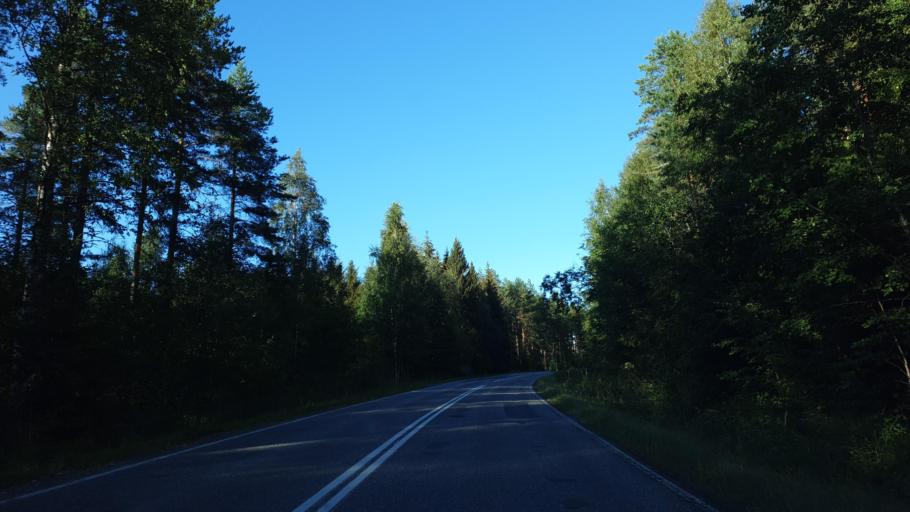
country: FI
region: Northern Savo
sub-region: Koillis-Savo
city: Juankoski
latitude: 63.0886
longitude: 28.3980
